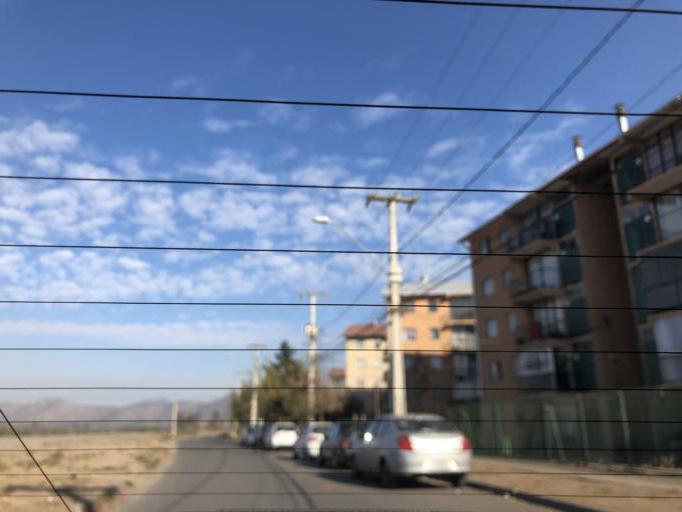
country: CL
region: Santiago Metropolitan
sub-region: Provincia de Cordillera
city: Puente Alto
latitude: -33.6324
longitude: -70.5904
